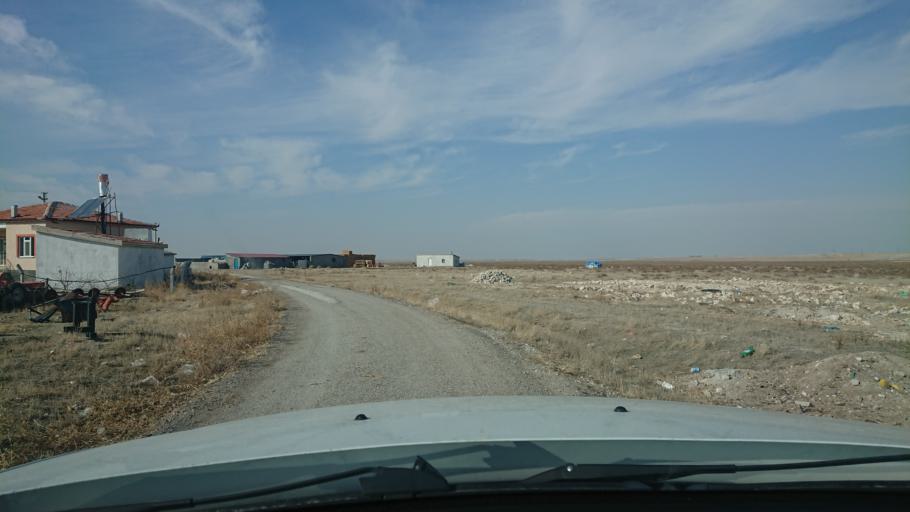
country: TR
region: Aksaray
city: Sultanhani
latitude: 38.2603
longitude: 33.4744
